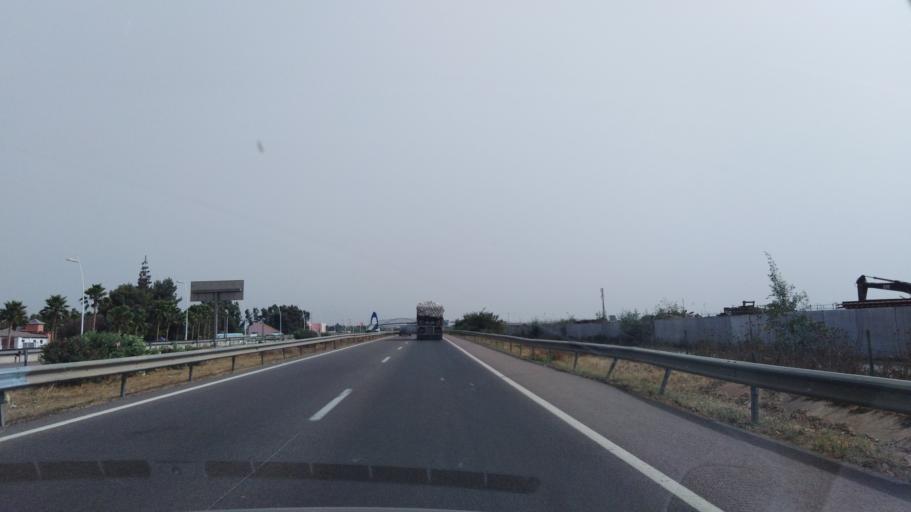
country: MA
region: Chaouia-Ouardigha
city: Nouaseur
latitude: 33.3787
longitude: -7.6217
